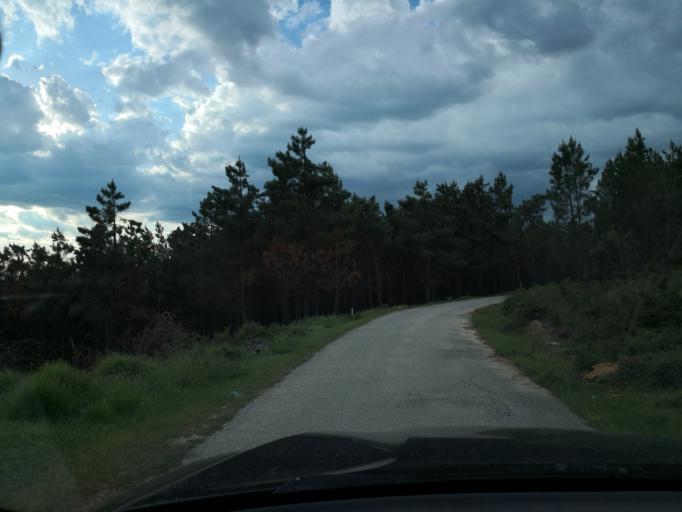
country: PT
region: Vila Real
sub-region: Sabrosa
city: Vilela
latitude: 41.2228
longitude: -7.6709
